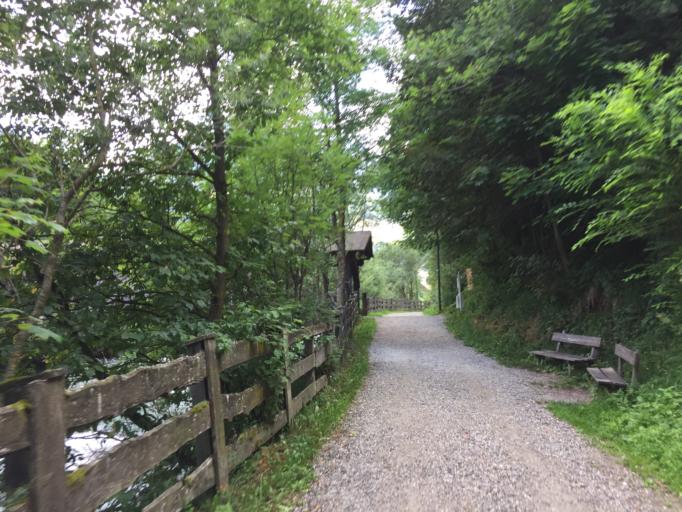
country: IT
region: Trentino-Alto Adige
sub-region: Bolzano
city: Molini di Tures
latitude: 46.9507
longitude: 11.9226
